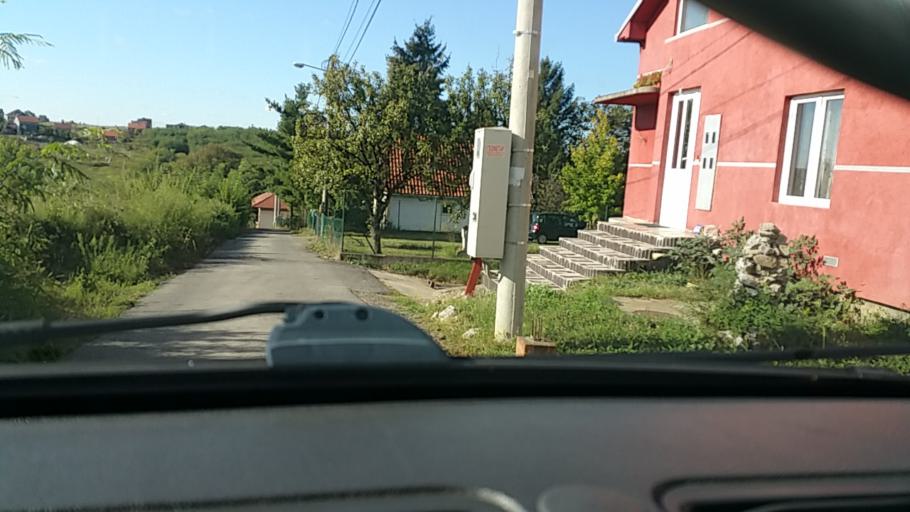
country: RS
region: Central Serbia
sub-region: Belgrade
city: Rakovica
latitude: 44.7335
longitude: 20.4629
